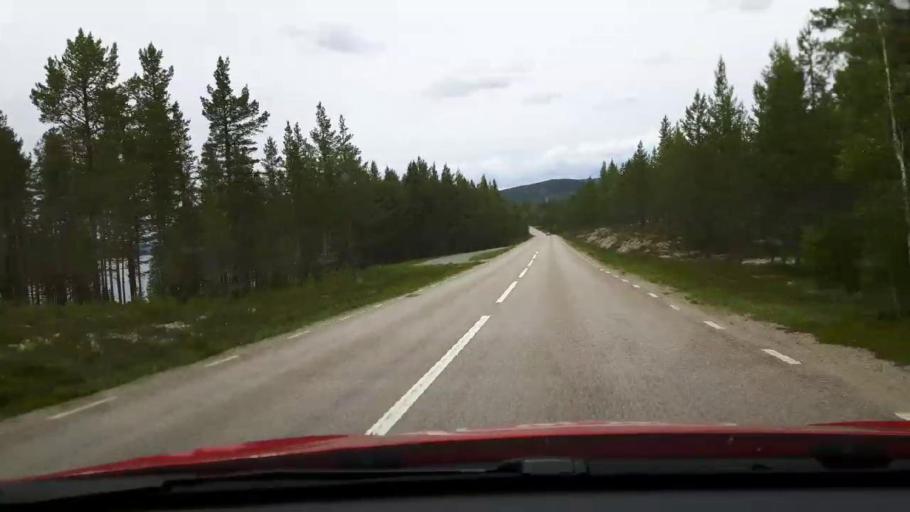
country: SE
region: Jaemtland
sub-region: Harjedalens Kommun
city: Sveg
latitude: 62.2573
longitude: 13.8399
